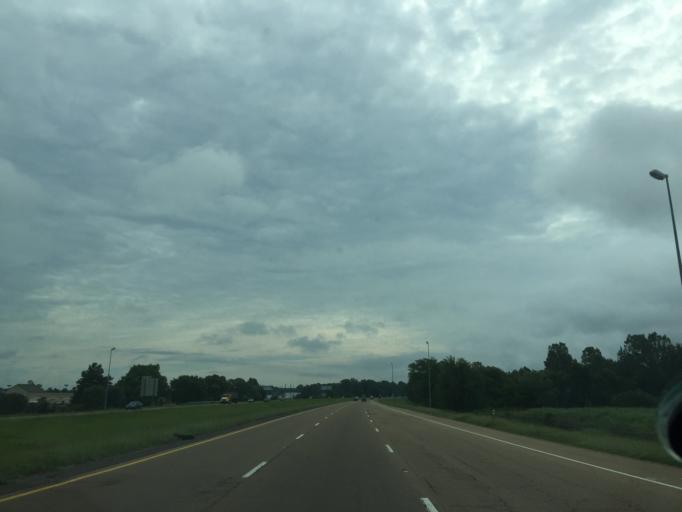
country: US
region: Mississippi
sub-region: Rankin County
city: Brandon
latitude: 32.2789
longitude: -90.0308
